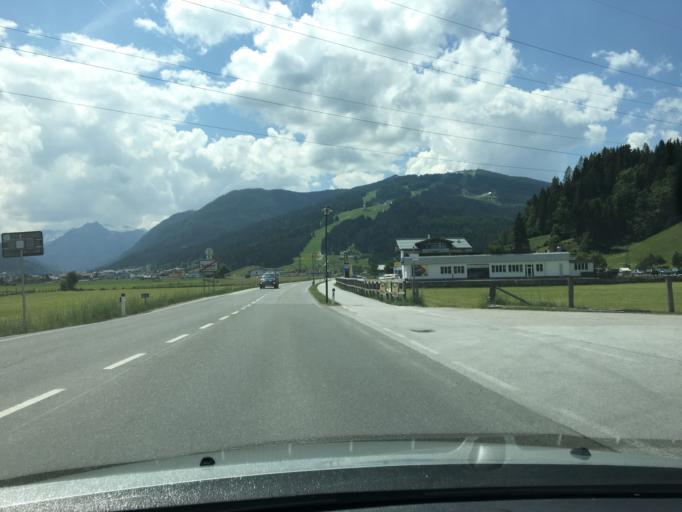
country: AT
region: Salzburg
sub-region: Politischer Bezirk Sankt Johann im Pongau
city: Flachau
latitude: 47.3700
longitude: 13.3871
